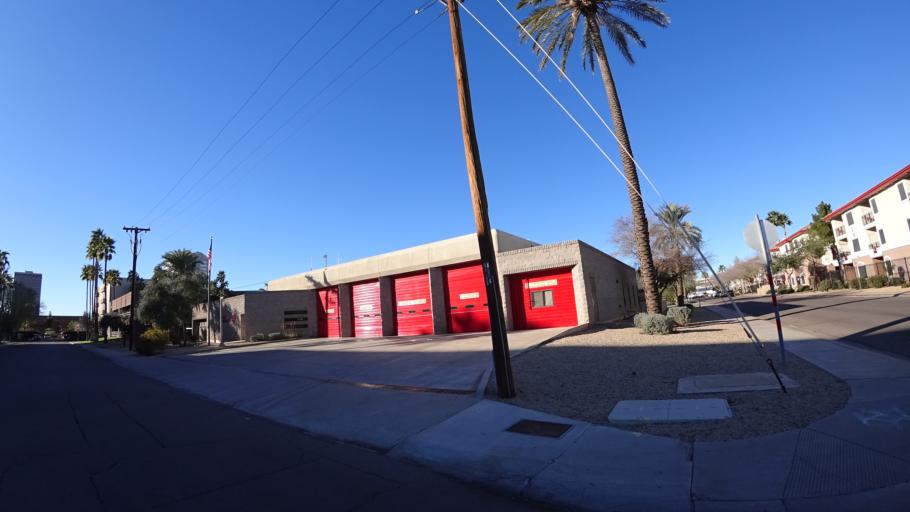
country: US
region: Arizona
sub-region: Maricopa County
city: Phoenix
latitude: 33.4928
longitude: -112.0681
